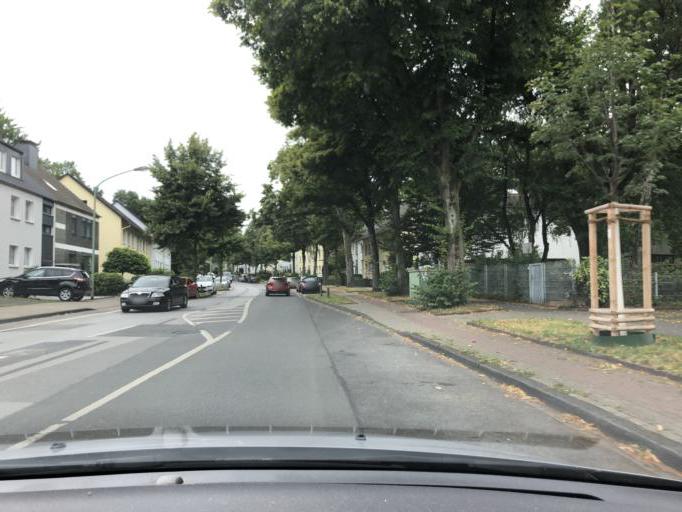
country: DE
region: North Rhine-Westphalia
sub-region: Regierungsbezirk Munster
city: Bottrop
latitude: 51.4663
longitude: 6.9442
